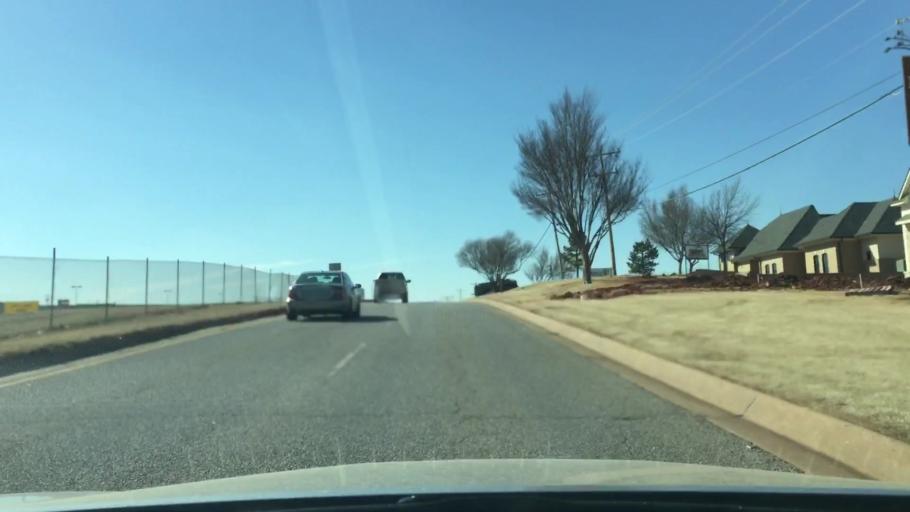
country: US
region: Oklahoma
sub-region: Oklahoma County
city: The Village
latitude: 35.6103
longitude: -97.6110
